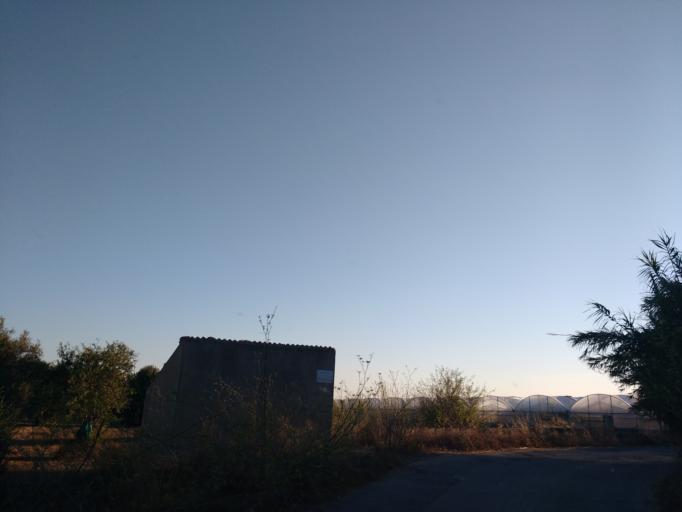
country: IT
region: Sicily
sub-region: Ragusa
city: Cava d'Aliga
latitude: 36.7321
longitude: 14.6987
